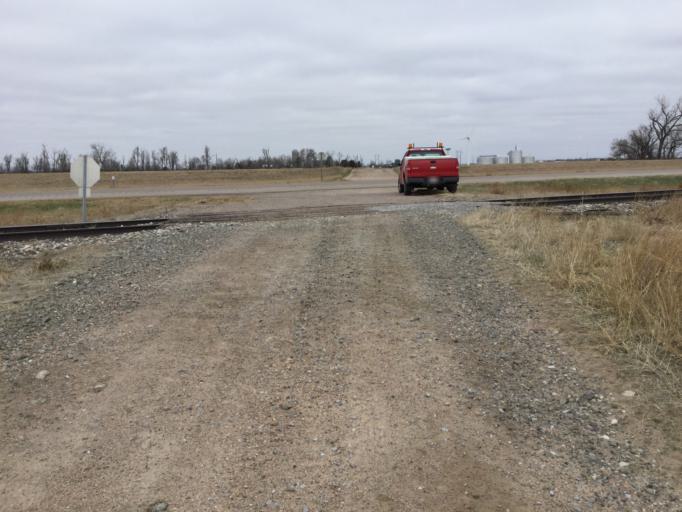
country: US
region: Kansas
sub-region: Barton County
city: Great Bend
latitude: 38.3372
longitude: -98.8294
